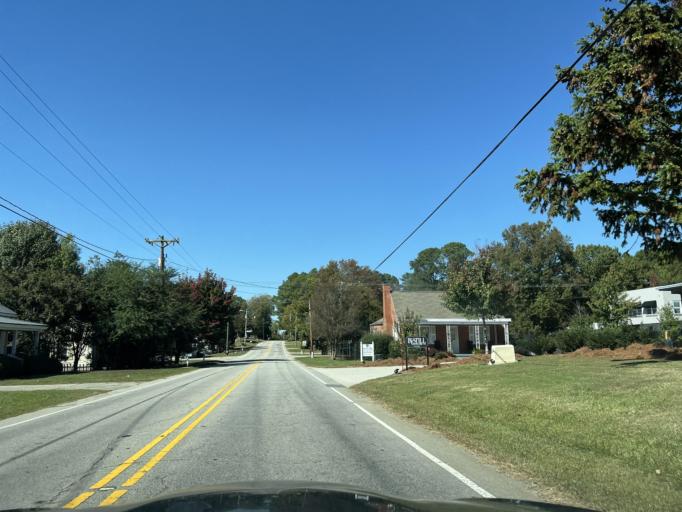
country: US
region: North Carolina
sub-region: Johnston County
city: Clayton
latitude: 35.6593
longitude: -78.4674
